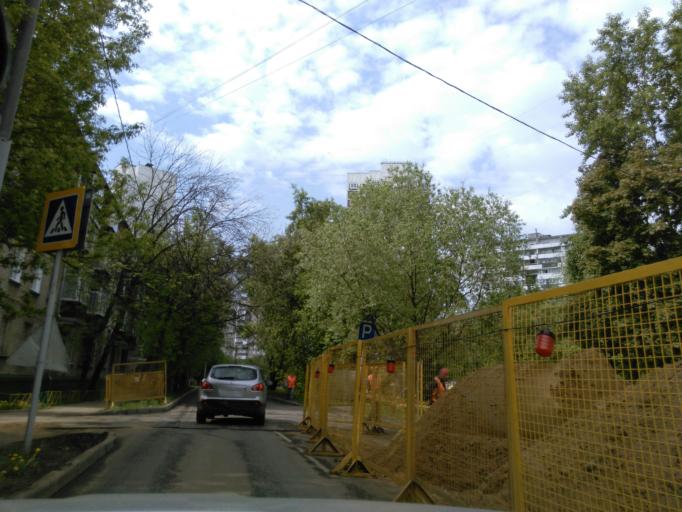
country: RU
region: Moscow
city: Novokhovrino
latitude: 55.8614
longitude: 37.5151
